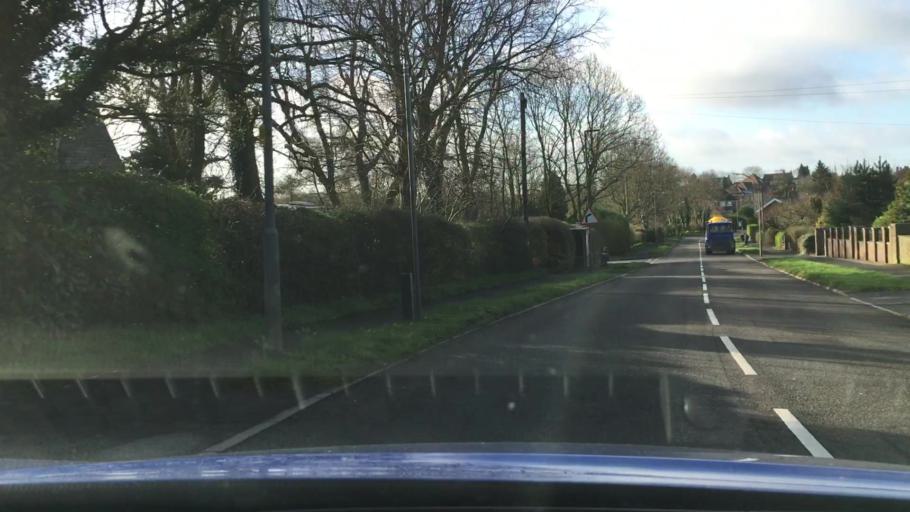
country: GB
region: England
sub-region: Derbyshire
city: Tibshelf
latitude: 53.1514
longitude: -1.3360
